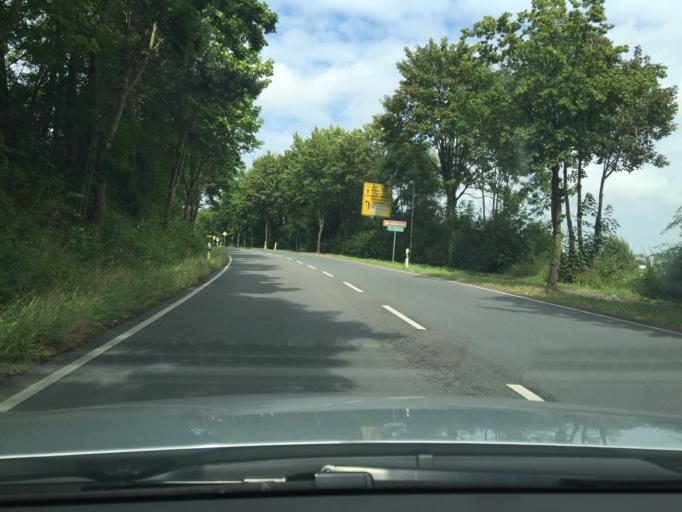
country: DE
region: North Rhine-Westphalia
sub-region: Regierungsbezirk Dusseldorf
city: Heiligenhaus
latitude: 51.3281
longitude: 6.9847
